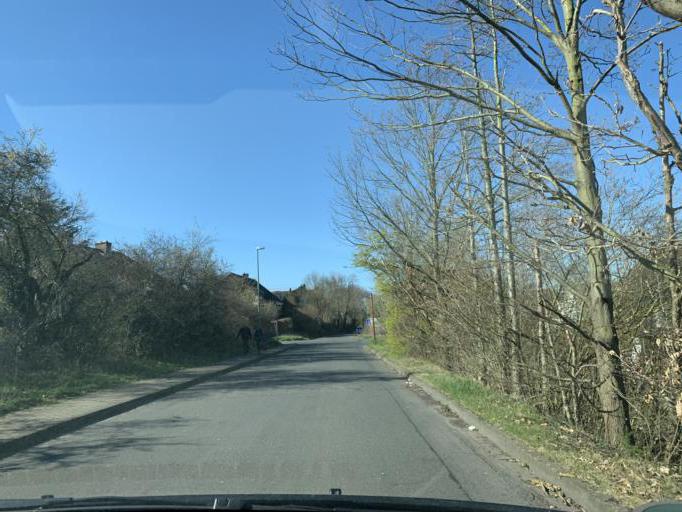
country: DE
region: North Rhine-Westphalia
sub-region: Regierungsbezirk Koln
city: Nideggen
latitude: 50.6950
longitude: 6.4882
